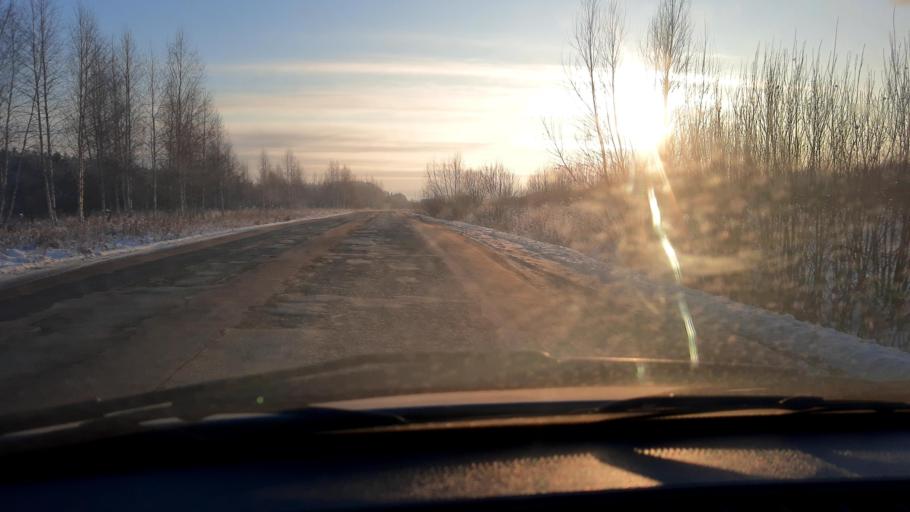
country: RU
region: Bashkortostan
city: Iglino
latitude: 54.7901
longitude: 56.3738
